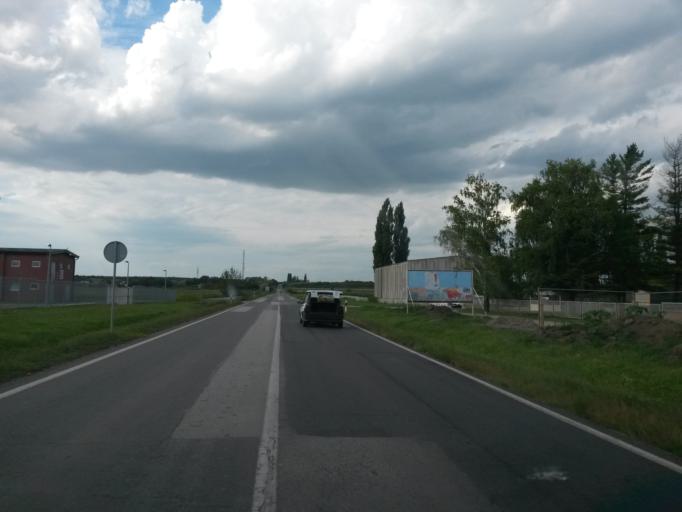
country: HR
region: Vukovarsko-Srijemska
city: Jarmina
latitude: 45.2940
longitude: 18.7398
